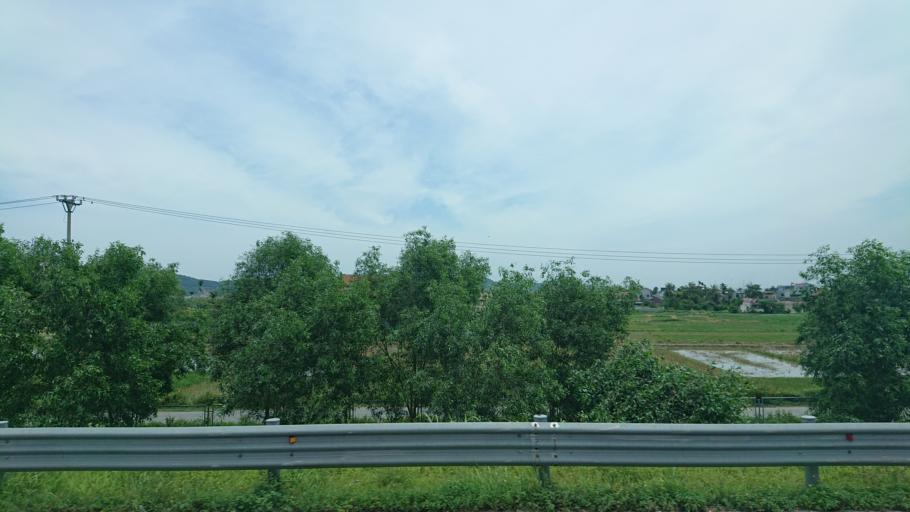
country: VN
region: Hai Phong
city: Nui Doi
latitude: 20.7703
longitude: 106.6237
